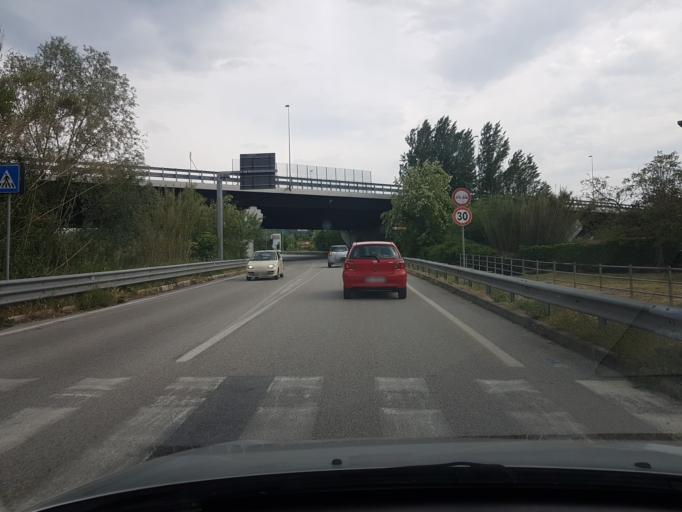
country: SI
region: Koper-Capodistria
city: Spodnje Skofije
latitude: 45.5894
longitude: 13.7983
